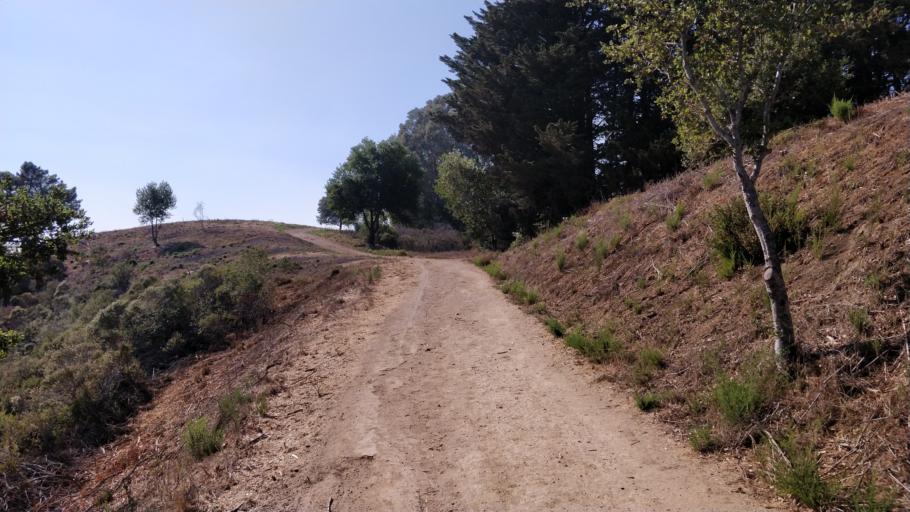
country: US
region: California
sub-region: Alameda County
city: Berkeley
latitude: 37.8699
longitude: -122.2314
